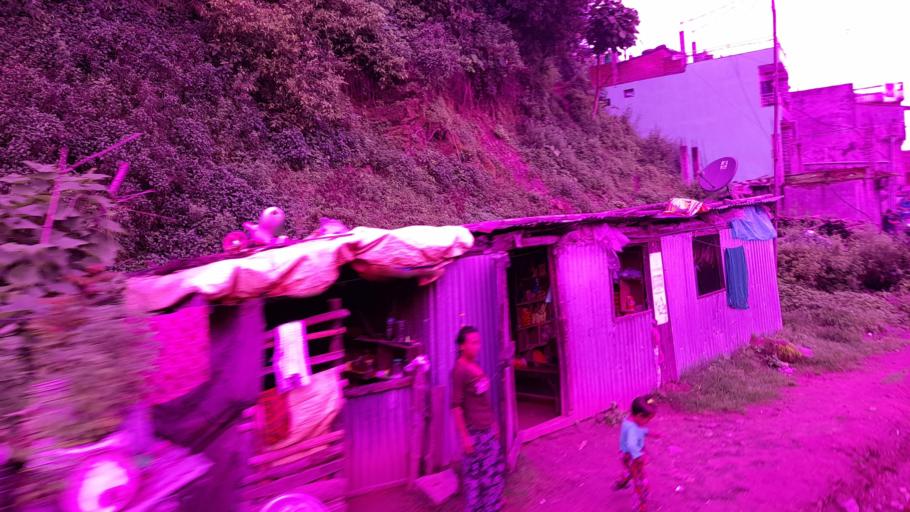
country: NP
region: Central Region
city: Kirtipur
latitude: 27.8276
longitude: 85.2093
